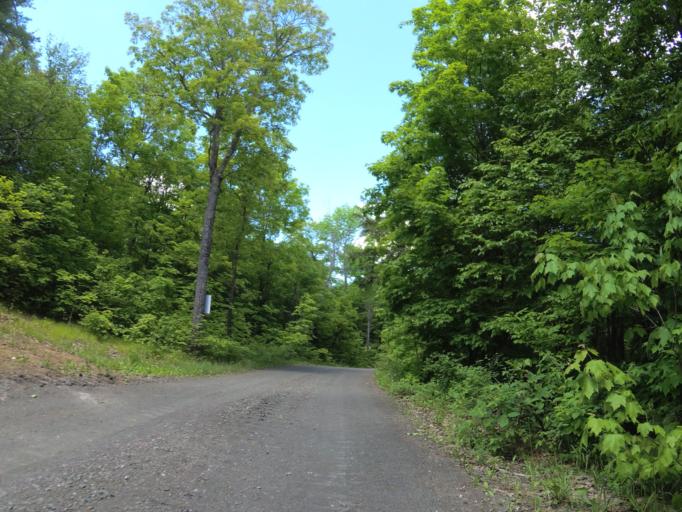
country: CA
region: Ontario
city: Renfrew
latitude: 45.0545
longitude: -76.8384
